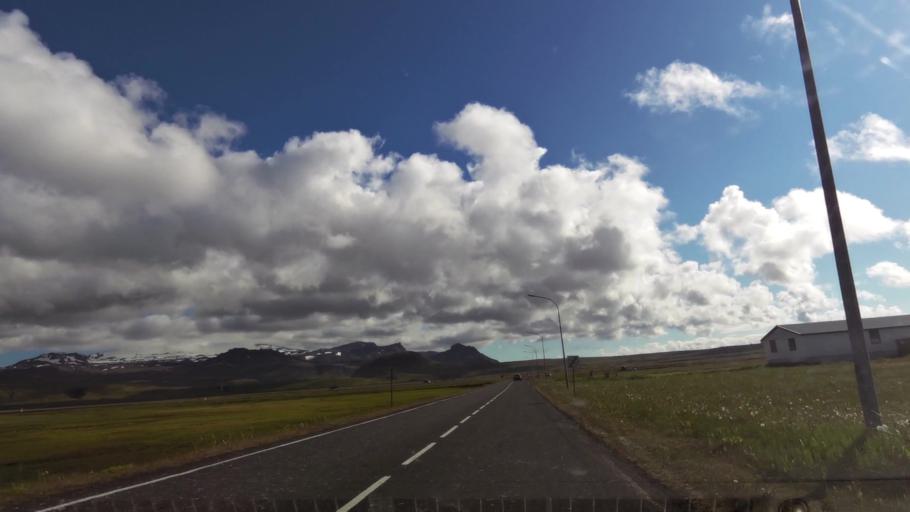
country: IS
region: West
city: Olafsvik
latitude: 64.9215
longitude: -23.8178
